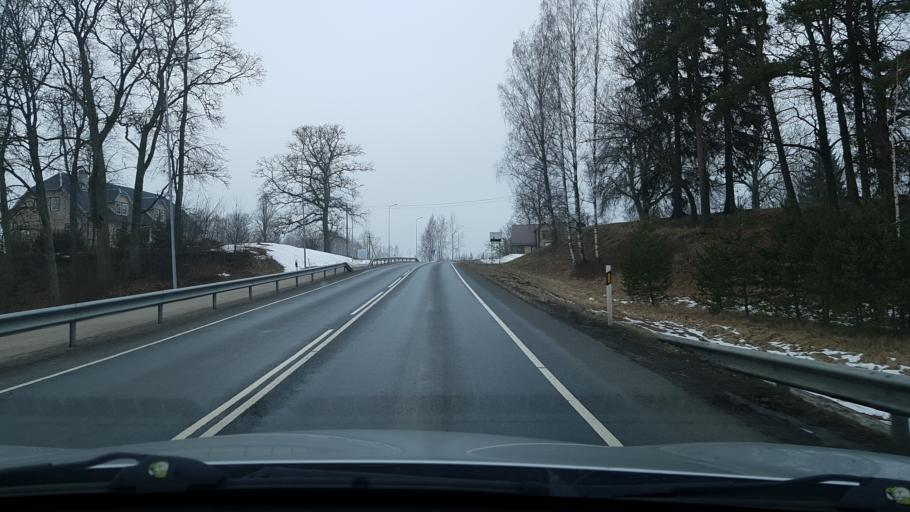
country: EE
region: Valgamaa
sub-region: Torva linn
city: Torva
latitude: 58.2294
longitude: 25.8837
